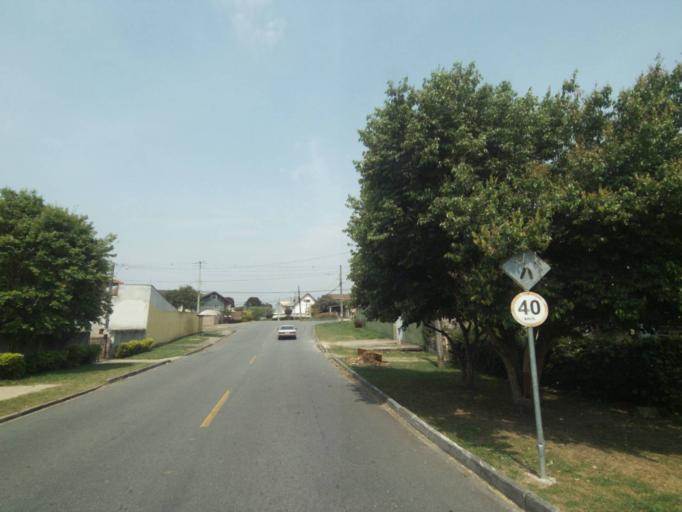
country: BR
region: Parana
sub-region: Sao Jose Dos Pinhais
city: Sao Jose dos Pinhais
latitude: -25.4919
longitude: -49.2114
